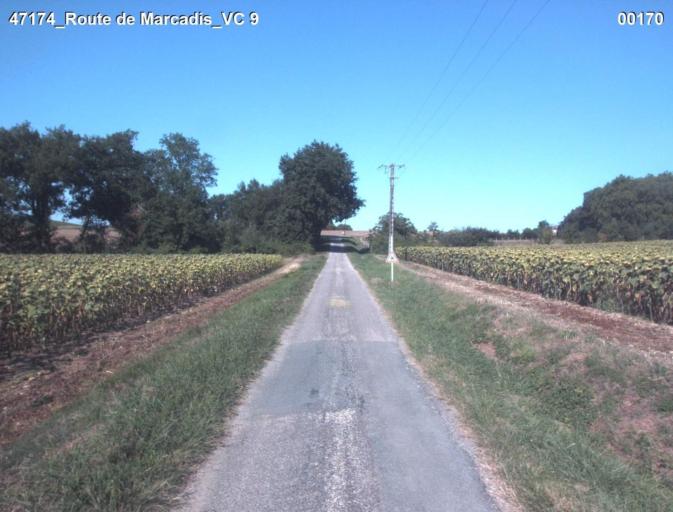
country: FR
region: Midi-Pyrenees
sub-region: Departement du Gers
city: Condom
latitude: 44.0196
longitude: 0.3363
